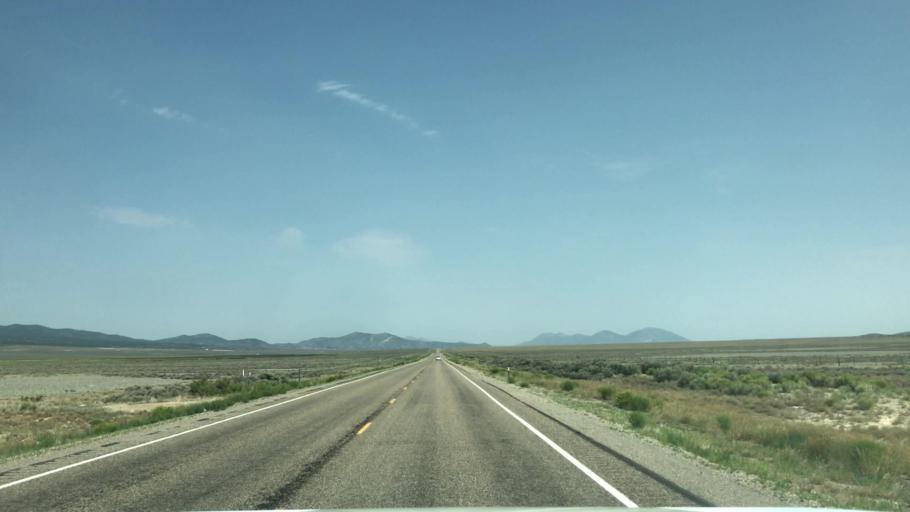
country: US
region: Nevada
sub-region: White Pine County
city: Ely
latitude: 39.1183
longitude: -114.7730
